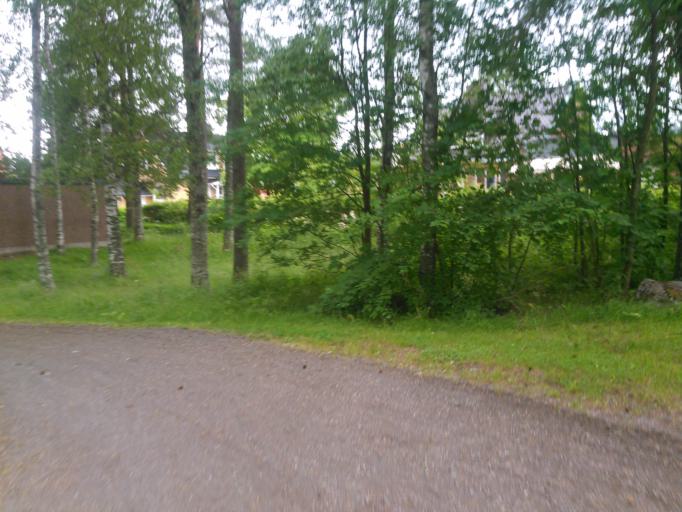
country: SE
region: Vaesterbotten
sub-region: Umea Kommun
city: Umea
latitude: 63.8066
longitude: 20.3045
